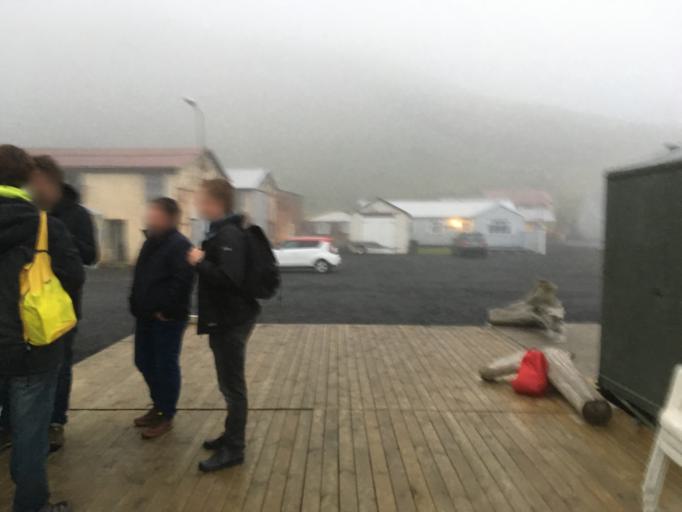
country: IS
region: South
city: Vestmannaeyjar
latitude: 63.4167
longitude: -19.0139
